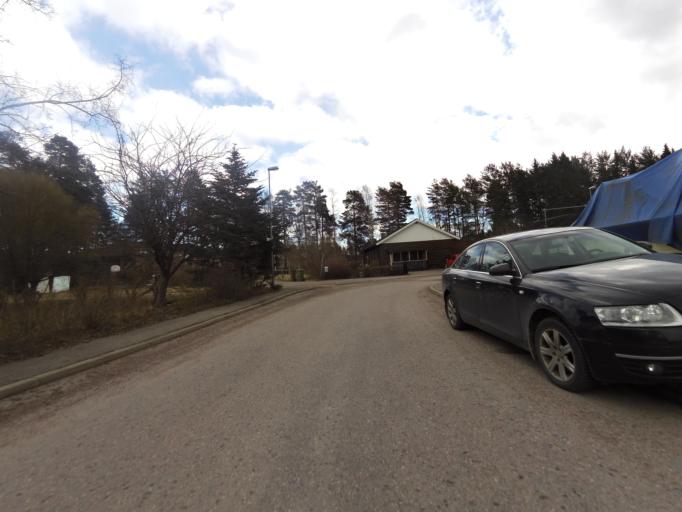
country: SE
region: Gaevleborg
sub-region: Gavle Kommun
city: Gavle
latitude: 60.6912
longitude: 17.0968
